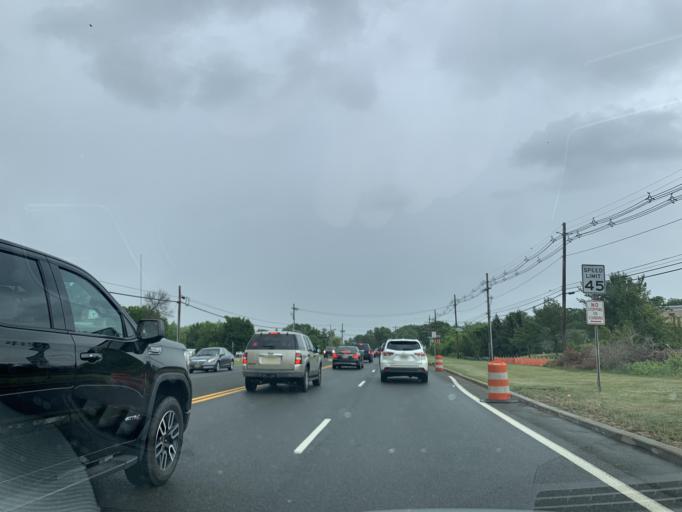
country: US
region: New Jersey
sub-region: Somerset County
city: Bloomingdale
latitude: 40.5186
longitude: -74.6311
